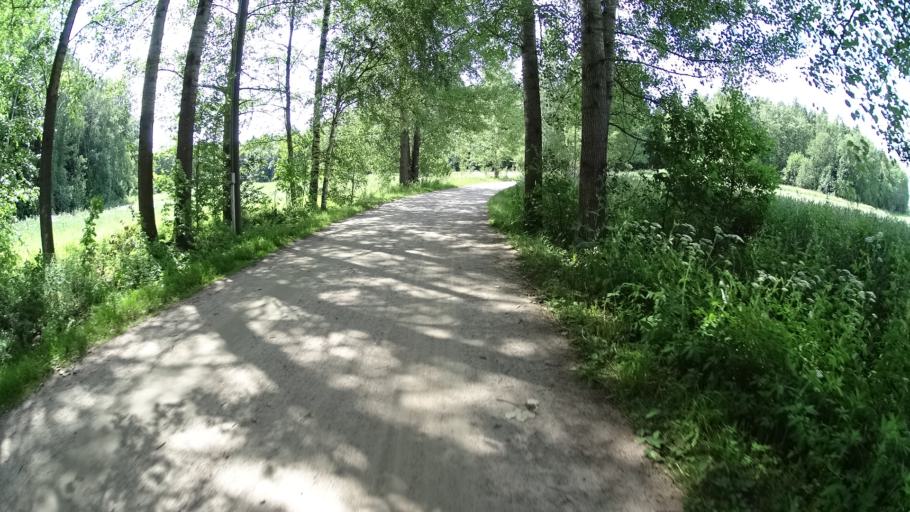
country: FI
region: Uusimaa
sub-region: Helsinki
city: Helsinki
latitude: 60.2719
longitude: 24.9317
